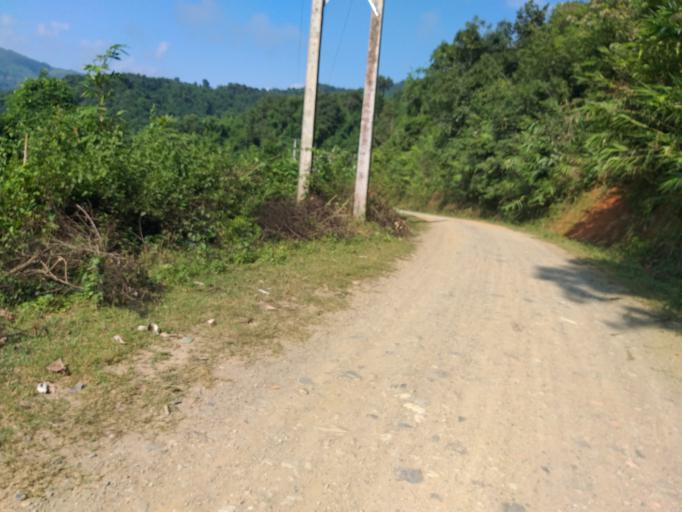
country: LA
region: Phongsali
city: Khoa
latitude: 21.1976
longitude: 102.6669
